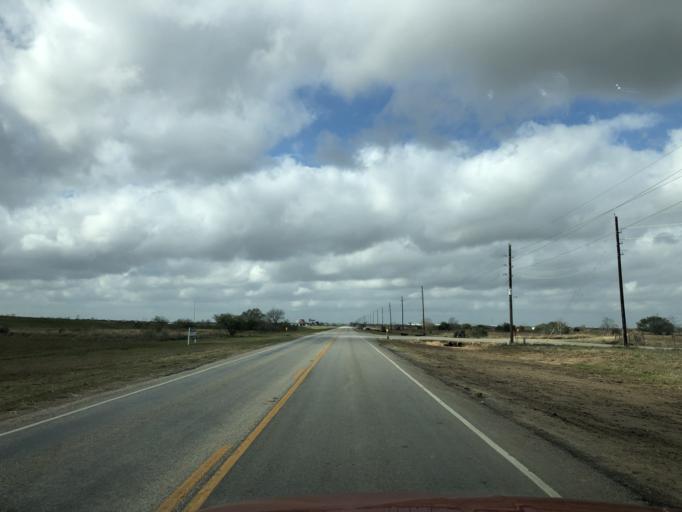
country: US
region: Texas
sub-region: Austin County
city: Sealy
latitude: 29.7648
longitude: -96.1871
